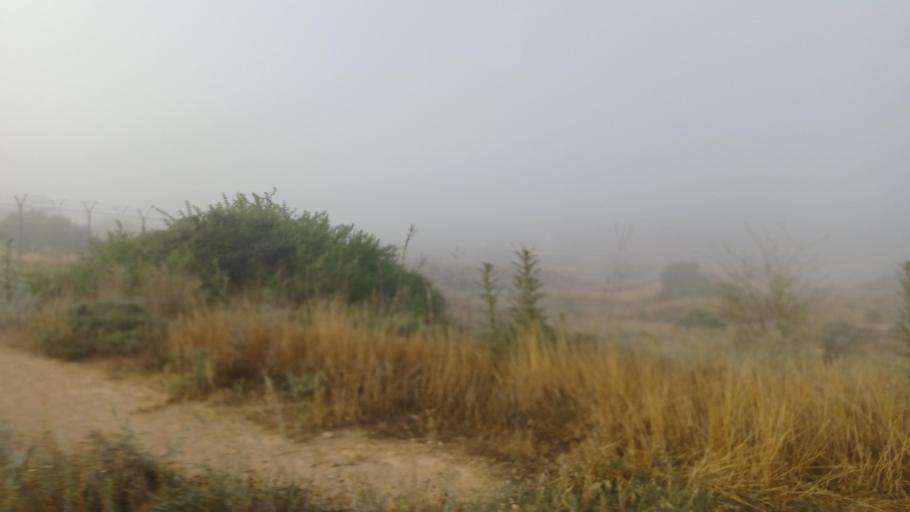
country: CY
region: Ammochostos
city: Acheritou
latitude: 35.0915
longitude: 33.8833
